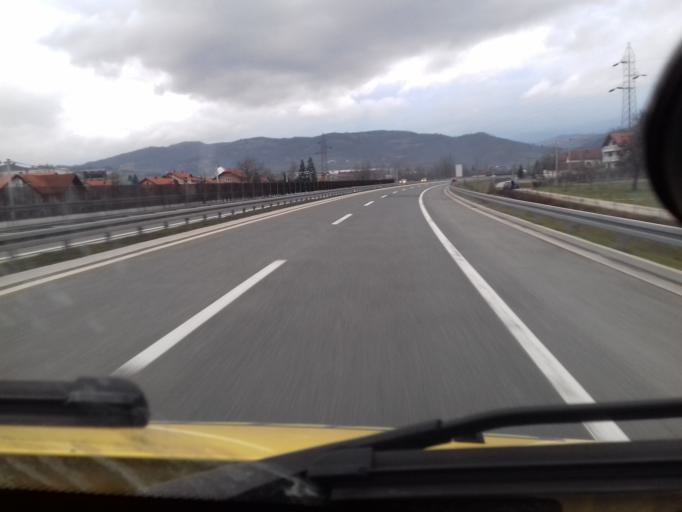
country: BA
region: Federation of Bosnia and Herzegovina
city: Ilijas
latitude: 43.9620
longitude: 18.2583
